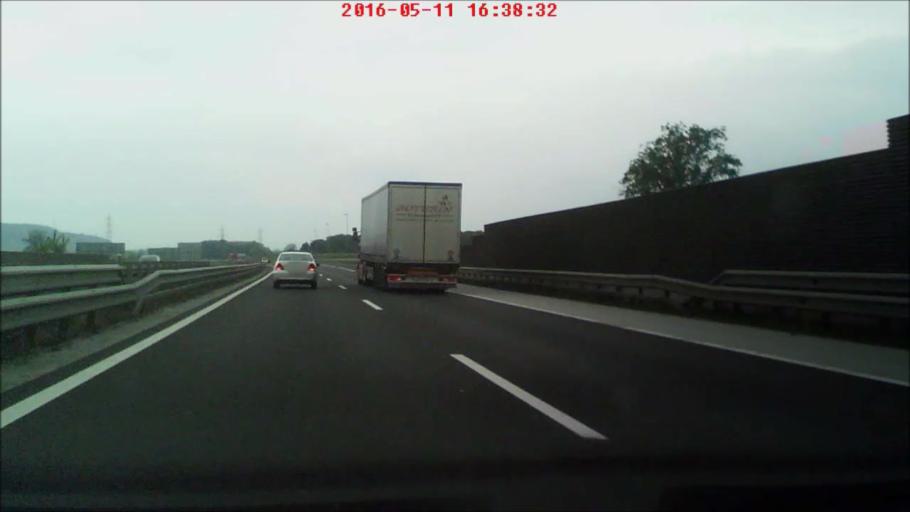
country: SI
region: Maribor
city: Maribor
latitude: 46.5508
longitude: 15.6915
